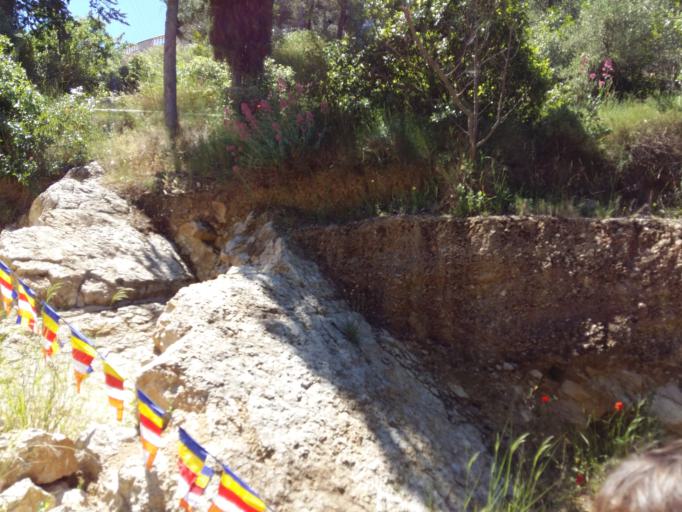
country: FR
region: Provence-Alpes-Cote d'Azur
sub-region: Departement des Bouches-du-Rhone
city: Marseille 11
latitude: 43.2804
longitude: 5.4660
